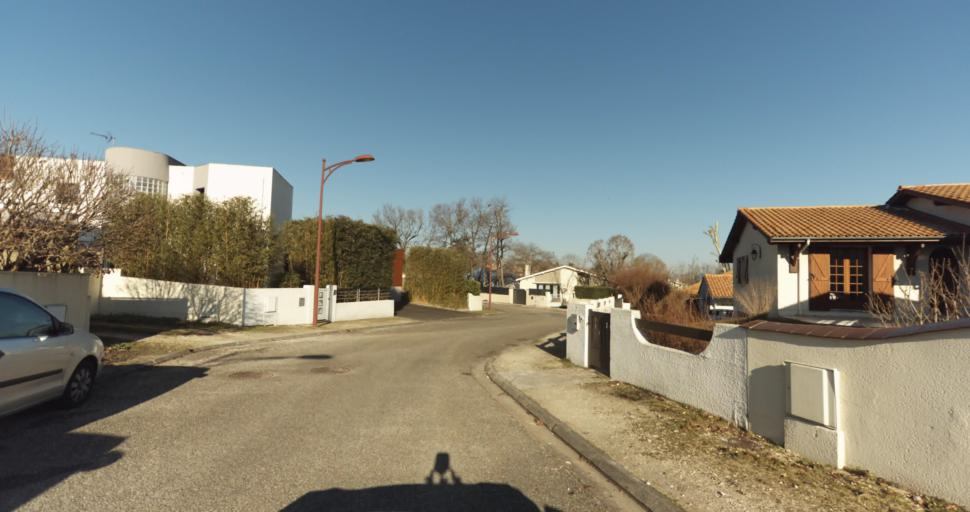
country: FR
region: Aquitaine
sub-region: Departement de la Gironde
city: Carbon-Blanc
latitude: 44.8943
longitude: -0.5078
